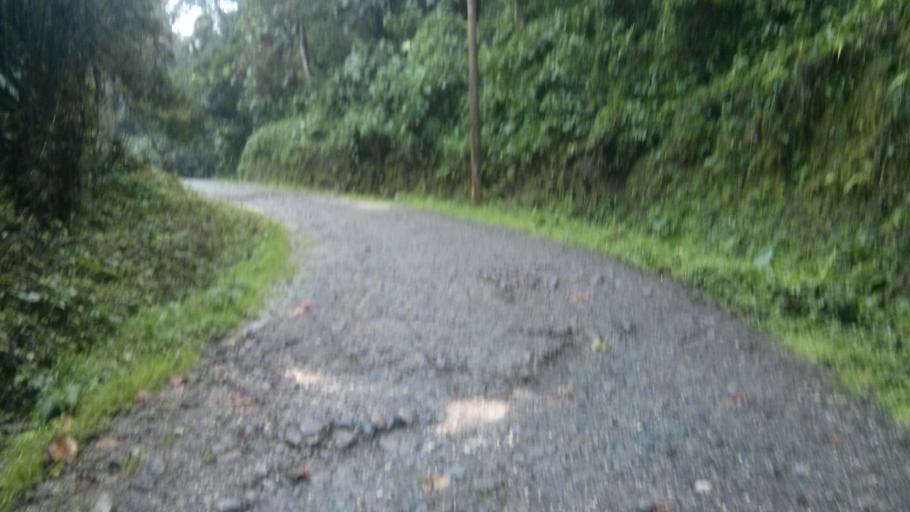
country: CR
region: San Jose
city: Ipis
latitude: 10.0282
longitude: -83.9413
